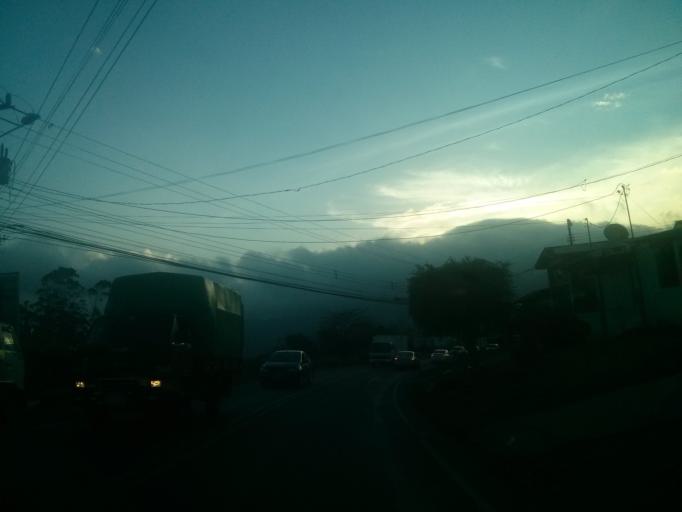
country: CR
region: Cartago
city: Cartago
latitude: 9.8770
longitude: -83.9265
